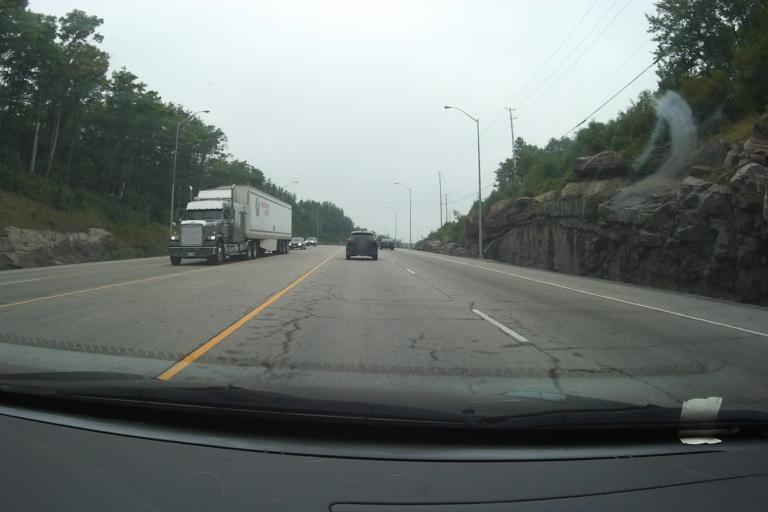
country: CA
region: Ontario
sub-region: Nipissing District
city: North Bay
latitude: 46.3429
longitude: -79.4704
